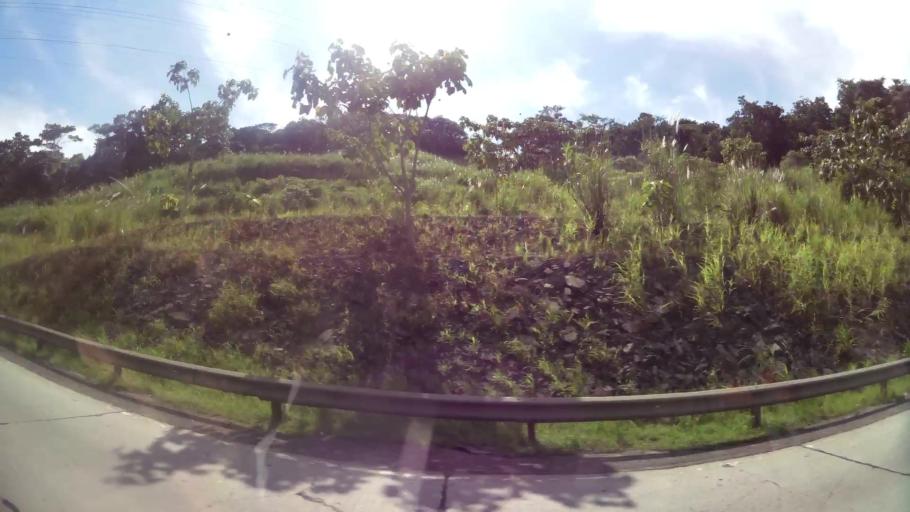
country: PA
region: Panama
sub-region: Distrito de Panama
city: Paraiso
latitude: 9.0290
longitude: -79.6138
